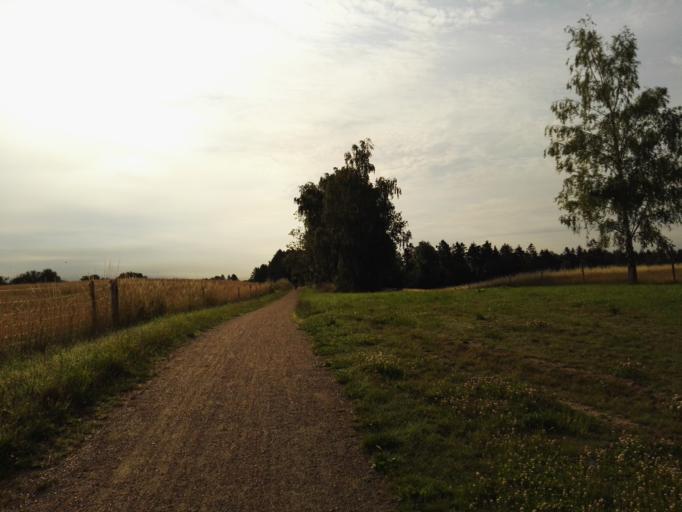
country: DK
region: Capital Region
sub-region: Ballerup Kommune
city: Ballerup
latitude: 55.7506
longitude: 12.3551
